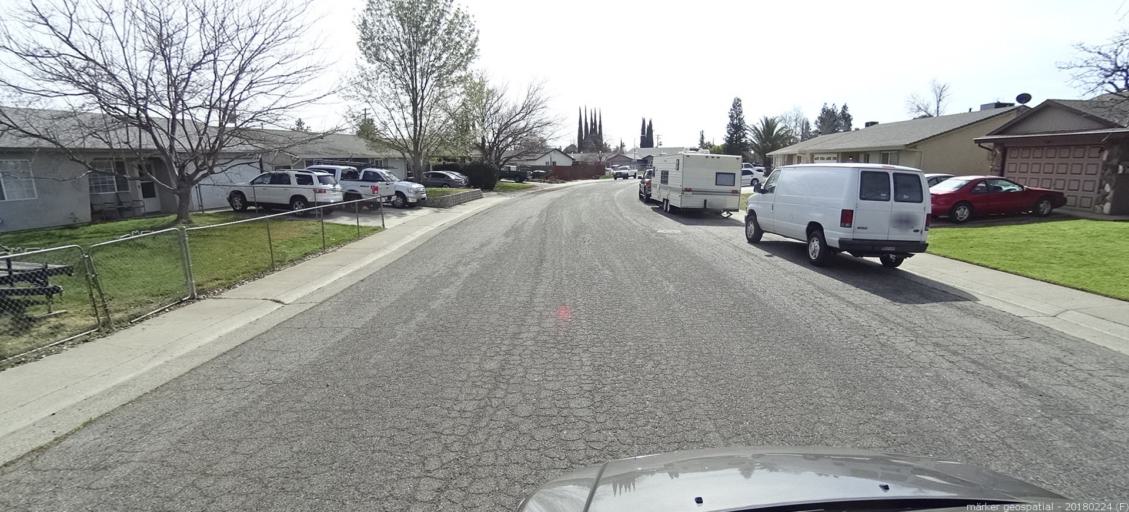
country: US
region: California
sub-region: Sacramento County
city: Rio Linda
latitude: 38.6781
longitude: -121.4429
